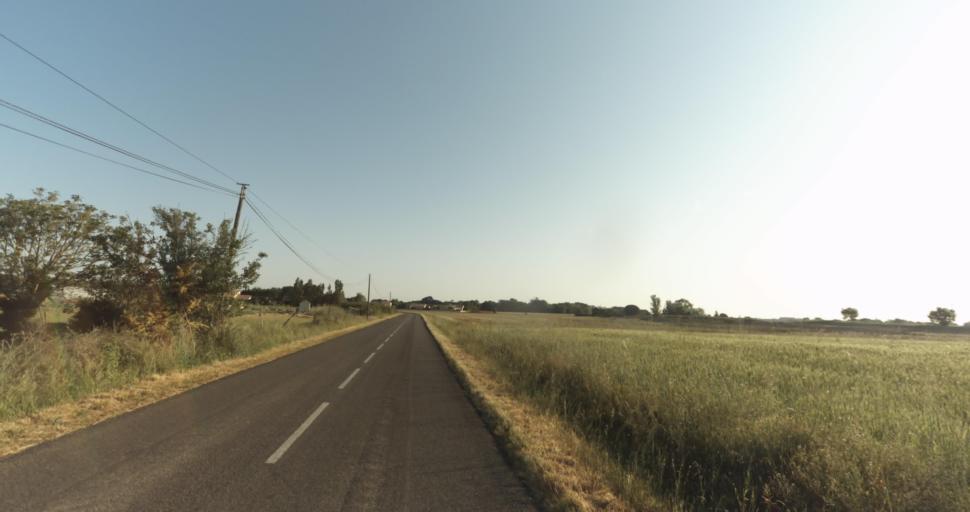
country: FR
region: Midi-Pyrenees
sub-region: Departement de la Haute-Garonne
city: Leguevin
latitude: 43.5842
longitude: 1.2368
